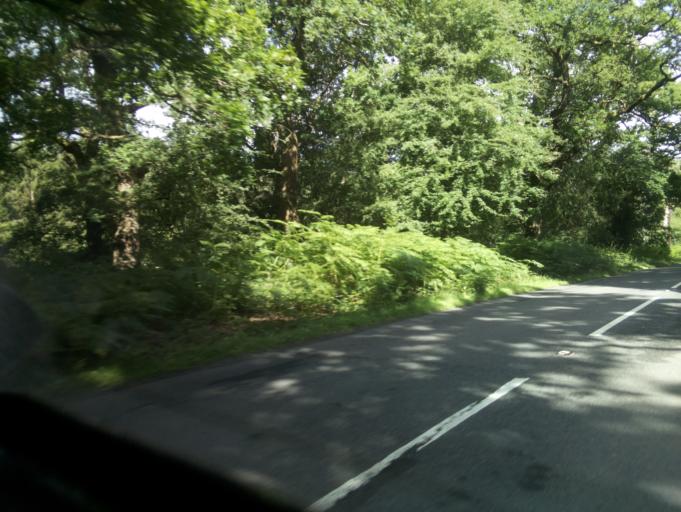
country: GB
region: England
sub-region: Gloucestershire
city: Bream
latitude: 51.7627
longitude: -2.5718
